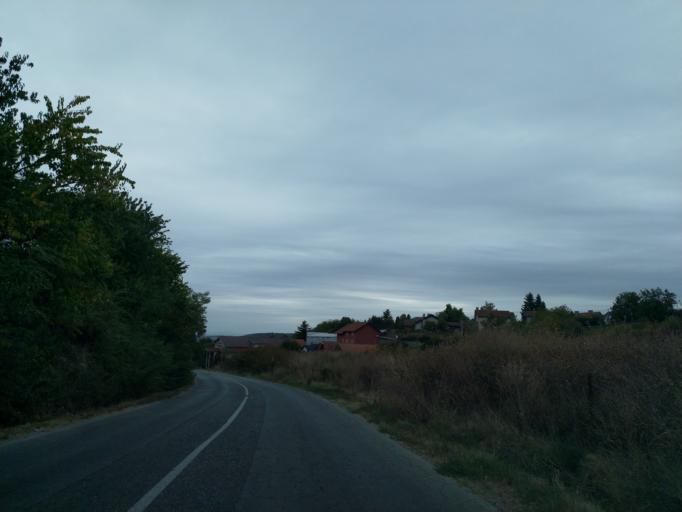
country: RS
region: Central Serbia
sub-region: Pomoravski Okrug
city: Jagodina
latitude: 43.9901
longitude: 21.2322
